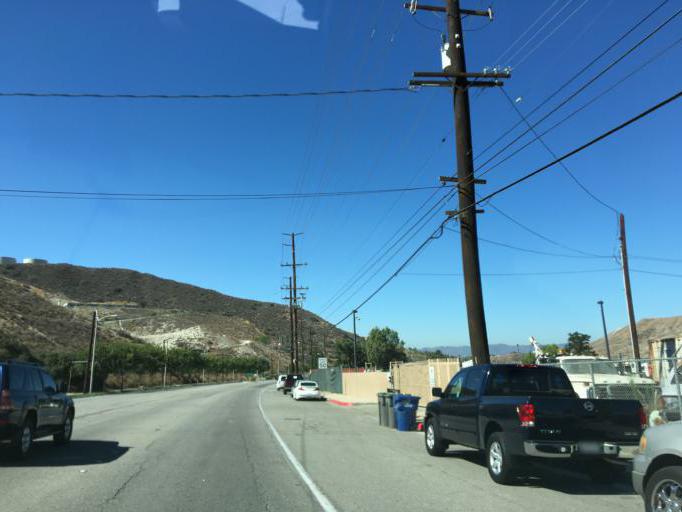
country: US
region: California
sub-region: Los Angeles County
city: Santa Clarita
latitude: 34.4378
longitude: -118.4321
